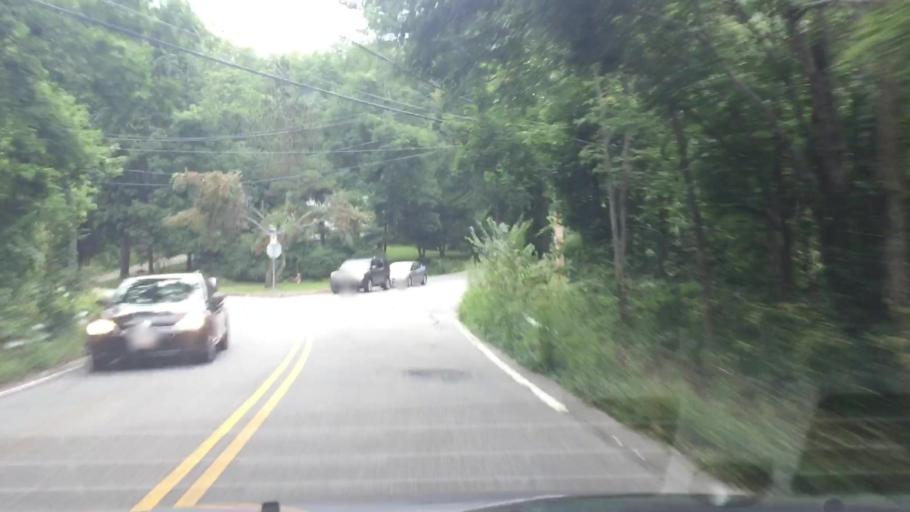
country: US
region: Massachusetts
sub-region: Essex County
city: North Andover
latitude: 42.7017
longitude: -71.0771
